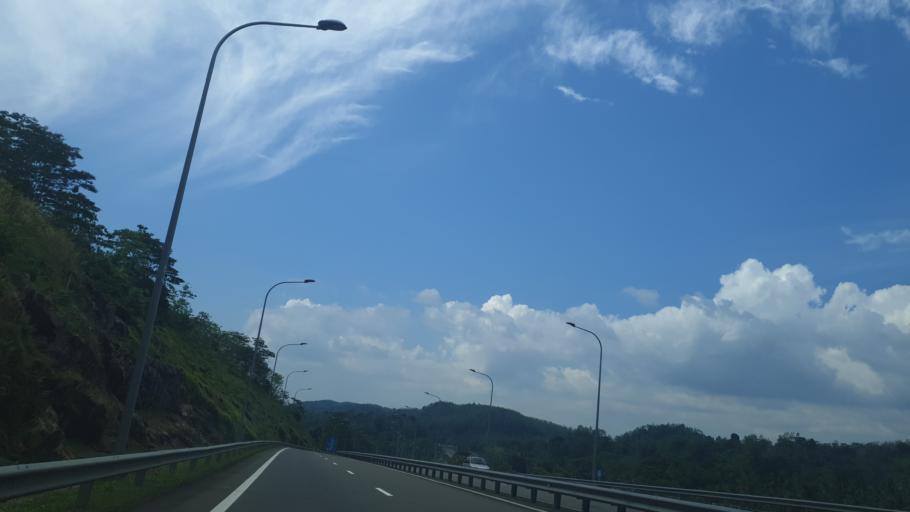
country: LK
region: Southern
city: Weligama
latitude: 6.0340
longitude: 80.3694
